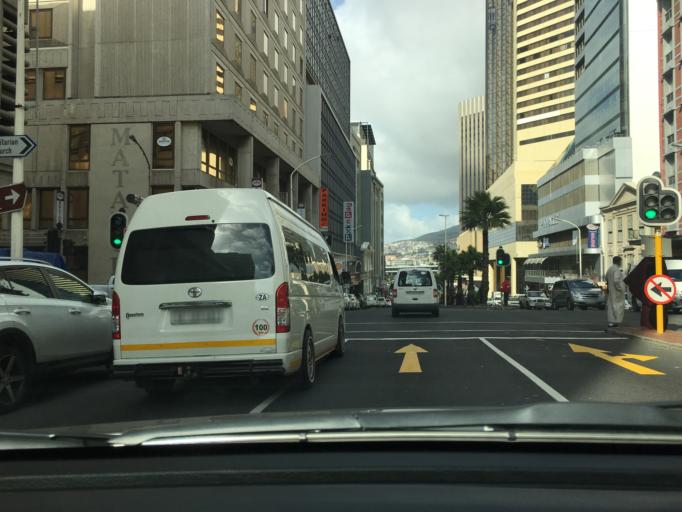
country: ZA
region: Western Cape
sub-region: City of Cape Town
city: Cape Town
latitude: -33.9204
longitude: 18.4210
